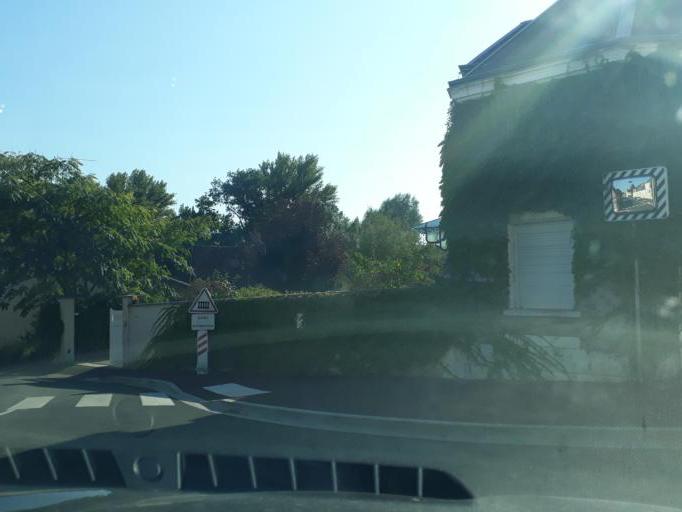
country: FR
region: Centre
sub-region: Departement du Loir-et-Cher
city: Thesee
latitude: 47.3239
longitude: 1.3101
